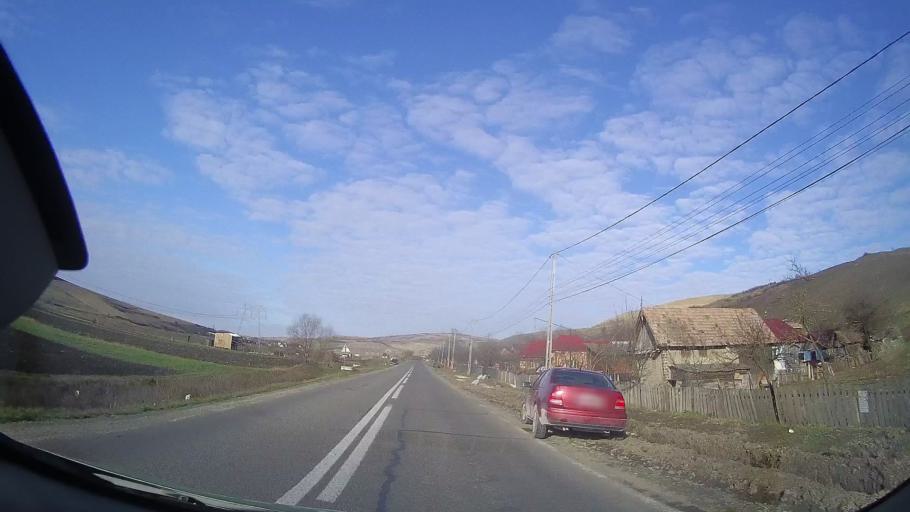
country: RO
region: Cluj
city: Caianu Mic
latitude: 46.8009
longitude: 23.8742
